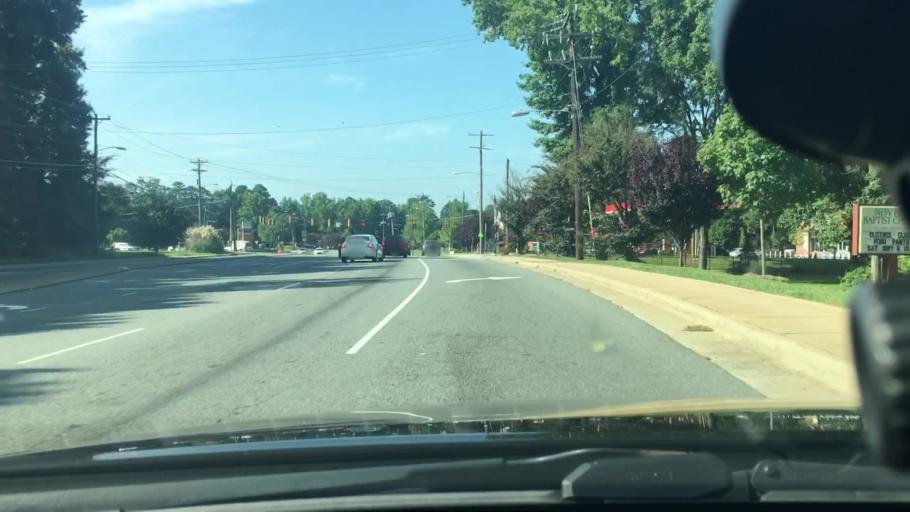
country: US
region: North Carolina
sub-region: Mecklenburg County
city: Matthews
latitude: 35.1872
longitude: -80.7296
